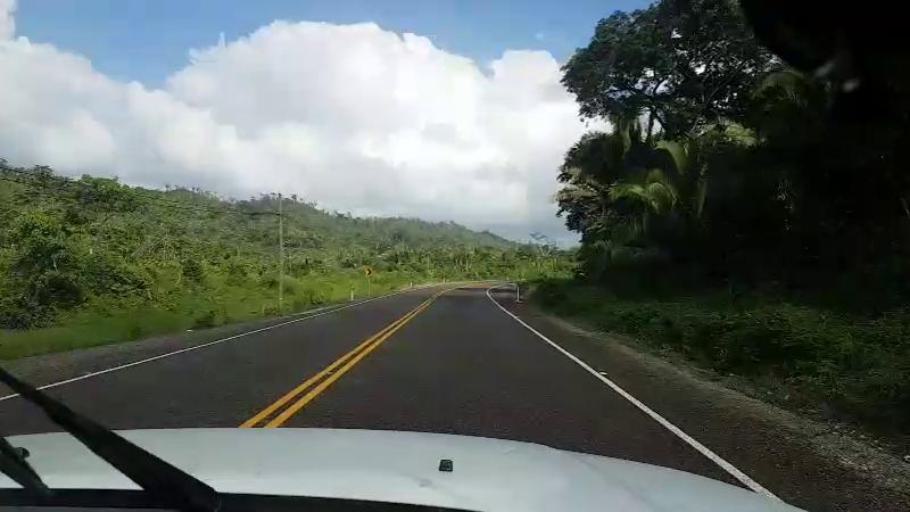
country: BZ
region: Cayo
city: Belmopan
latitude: 17.1478
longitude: -88.7254
